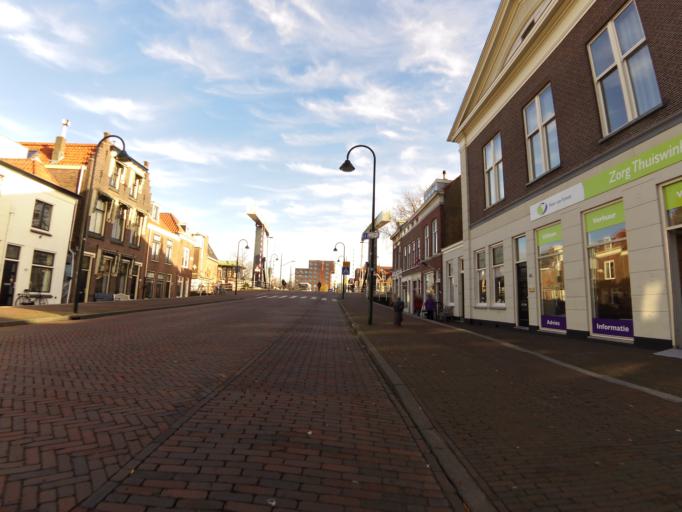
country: NL
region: South Holland
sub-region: Gemeente Delft
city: Delft
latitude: 52.0136
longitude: 4.3646
